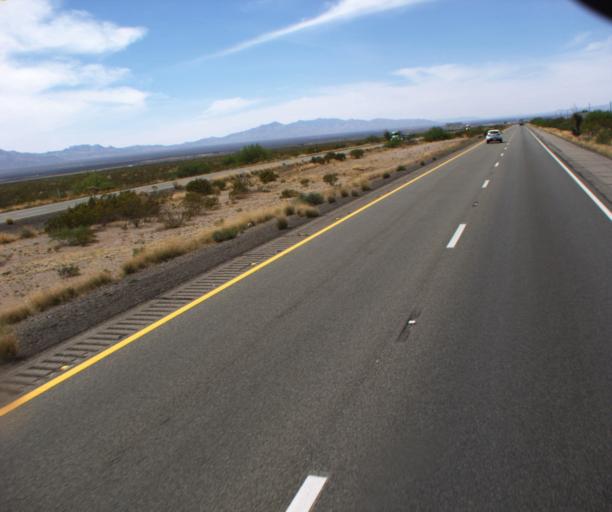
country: US
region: New Mexico
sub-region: Hidalgo County
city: Lordsburg
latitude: 32.2440
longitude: -109.1194
